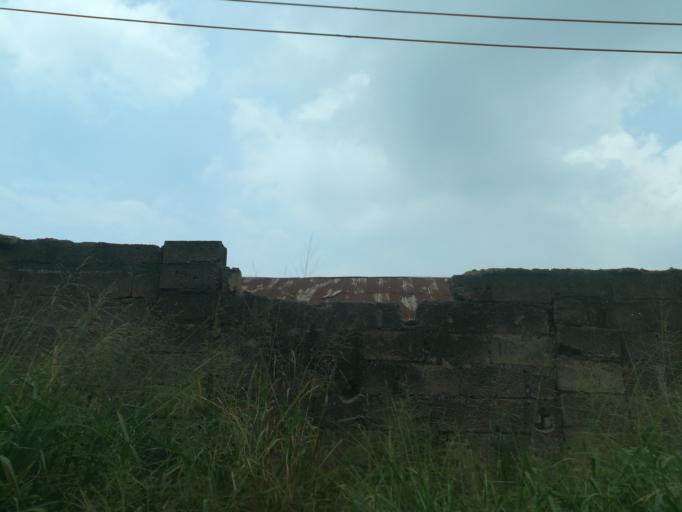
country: NG
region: Lagos
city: Ikorodu
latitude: 6.6194
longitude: 3.5191
